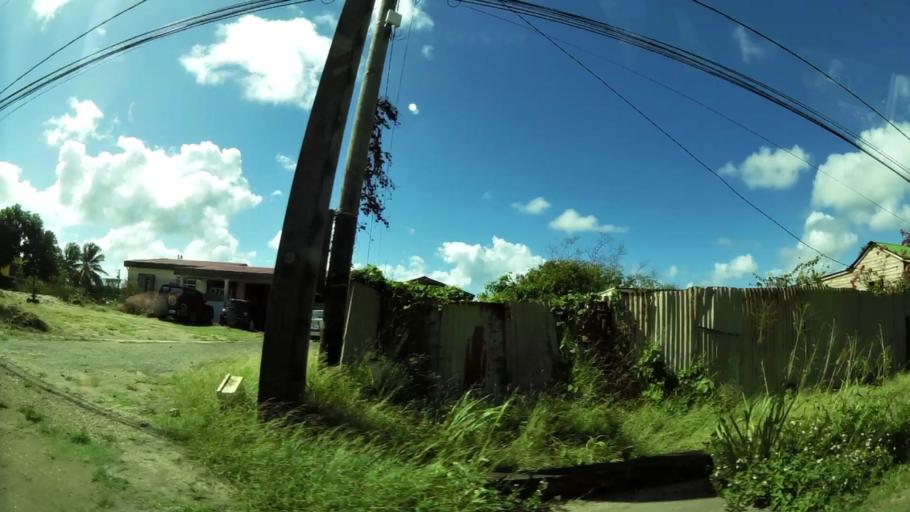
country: GP
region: Guadeloupe
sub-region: Guadeloupe
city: Petit-Canal
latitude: 16.3980
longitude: -61.4636
